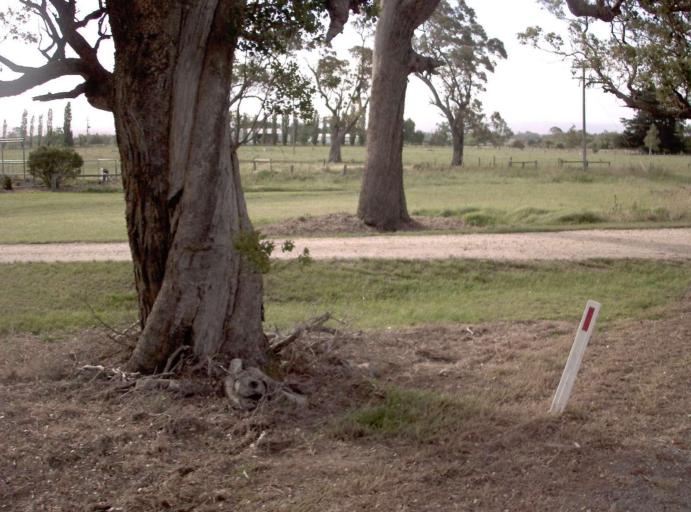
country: AU
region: Victoria
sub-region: Wellington
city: Heyfield
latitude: -37.9917
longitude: 146.7761
